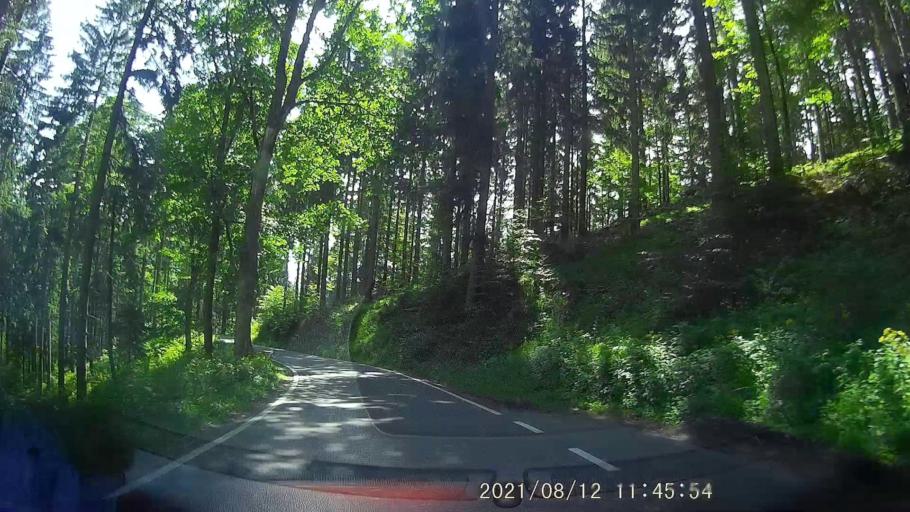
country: PL
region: Lower Silesian Voivodeship
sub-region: Powiat klodzki
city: Stronie Slaskie
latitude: 50.2506
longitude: 16.8434
